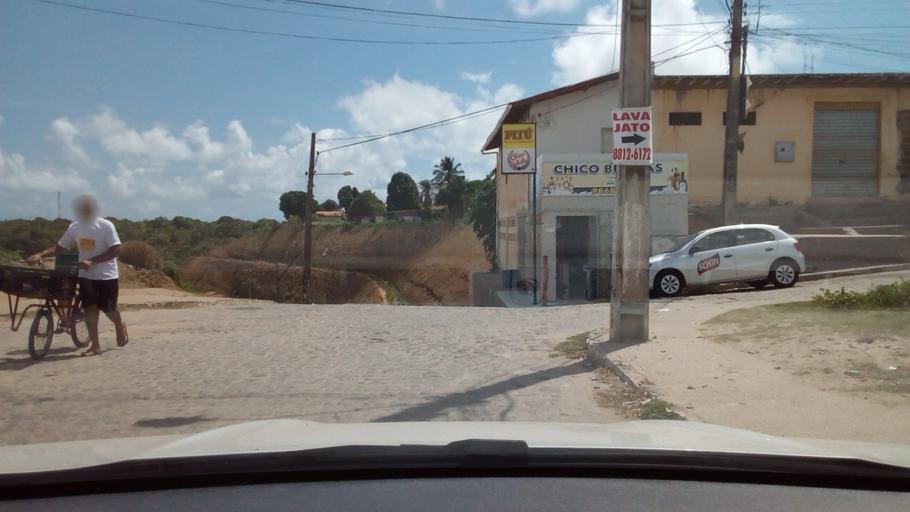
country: BR
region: Paraiba
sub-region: Joao Pessoa
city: Joao Pessoa
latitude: -7.1494
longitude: -34.8299
